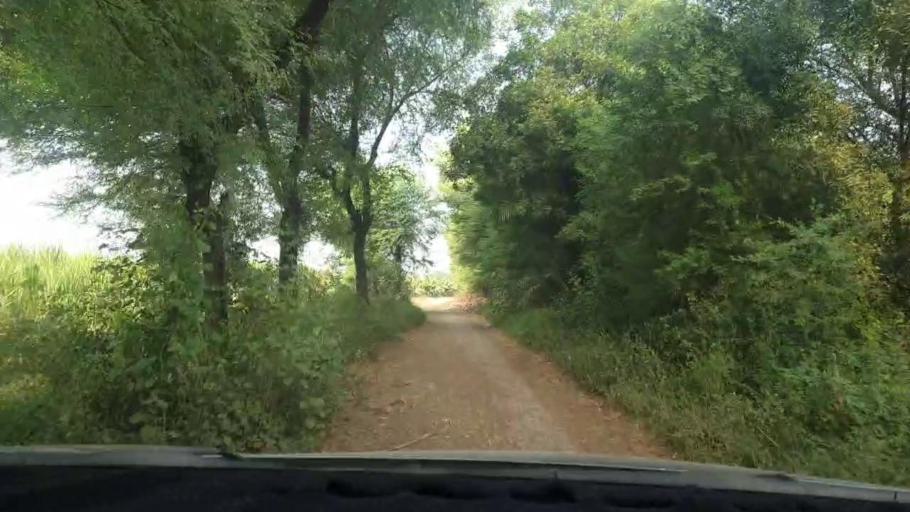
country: PK
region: Sindh
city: Matiari
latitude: 25.6015
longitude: 68.5501
